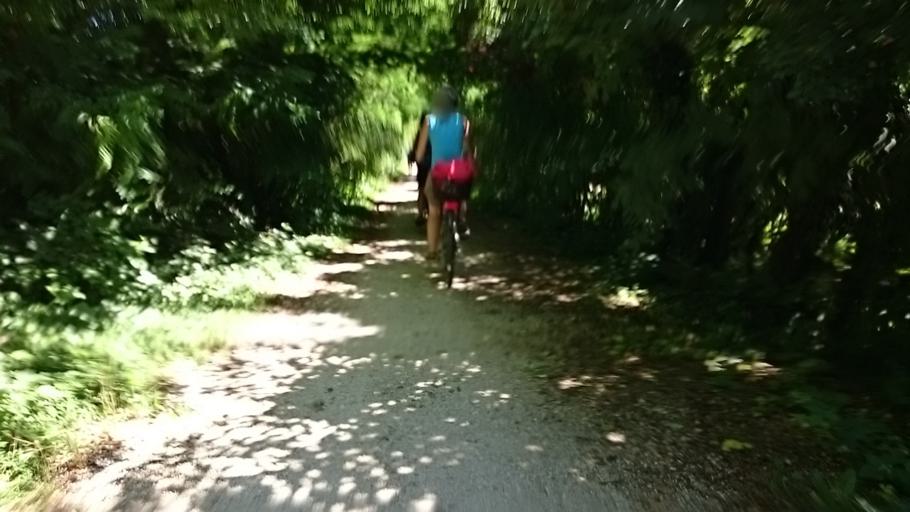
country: IT
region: Veneto
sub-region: Provincia di Treviso
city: Badoere
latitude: 45.6310
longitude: 12.1030
